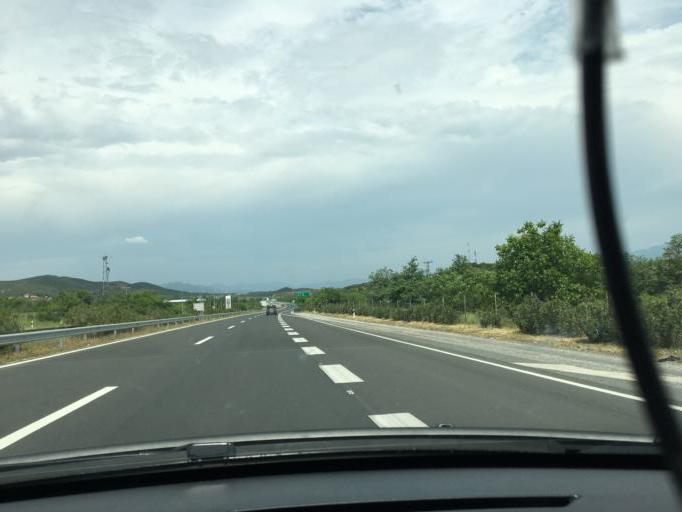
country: MK
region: Gevgelija
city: Miravci
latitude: 41.2485
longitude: 22.4818
